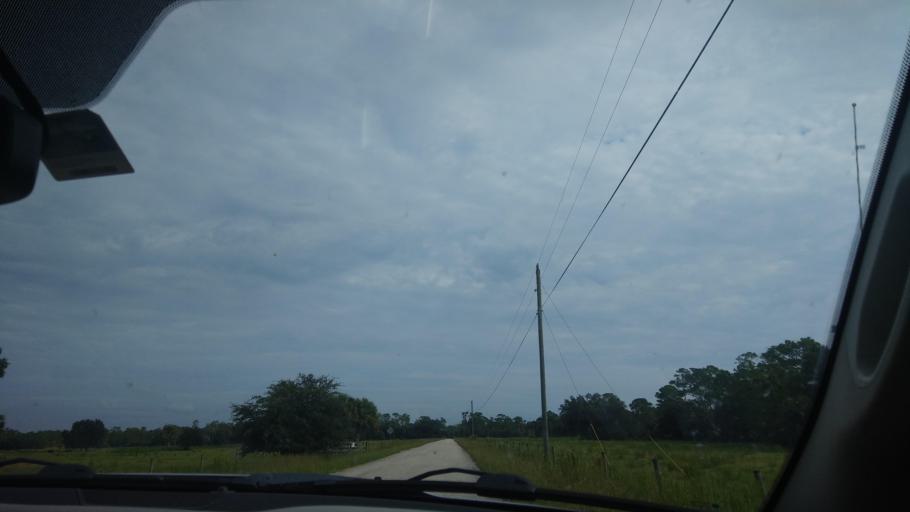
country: US
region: Florida
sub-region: Indian River County
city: Fellsmere
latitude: 27.6811
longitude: -80.7973
